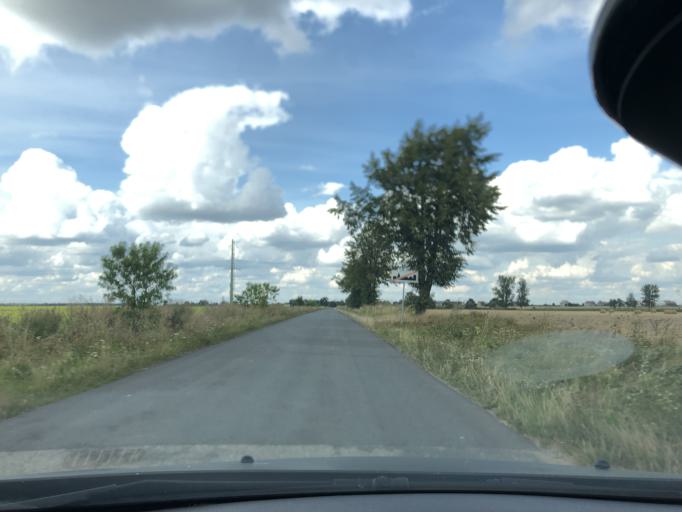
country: PL
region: Lodz Voivodeship
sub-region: Powiat wieruszowski
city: Walichnowy
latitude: 51.2387
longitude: 18.3879
